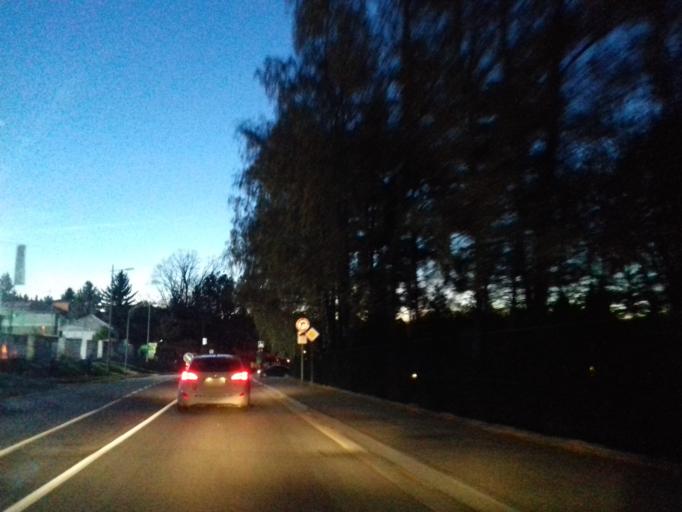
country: CZ
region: Vysocina
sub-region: Okres Pelhrimov
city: Humpolec
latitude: 49.5358
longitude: 15.3618
